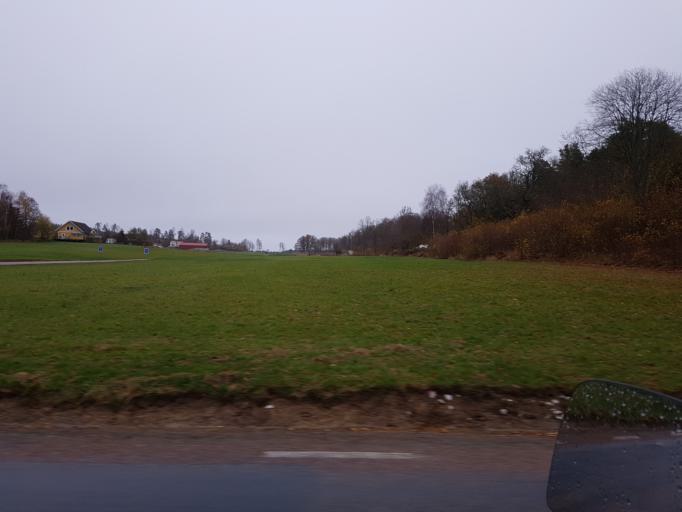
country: SE
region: Vaestra Goetaland
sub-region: Orust
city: Henan
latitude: 58.2849
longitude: 11.7134
